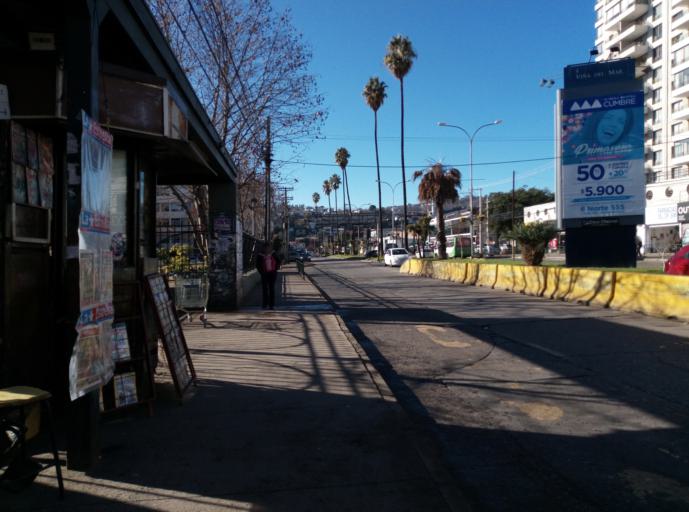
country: CL
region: Valparaiso
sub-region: Provincia de Valparaiso
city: Vina del Mar
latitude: -33.0084
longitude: -71.5456
